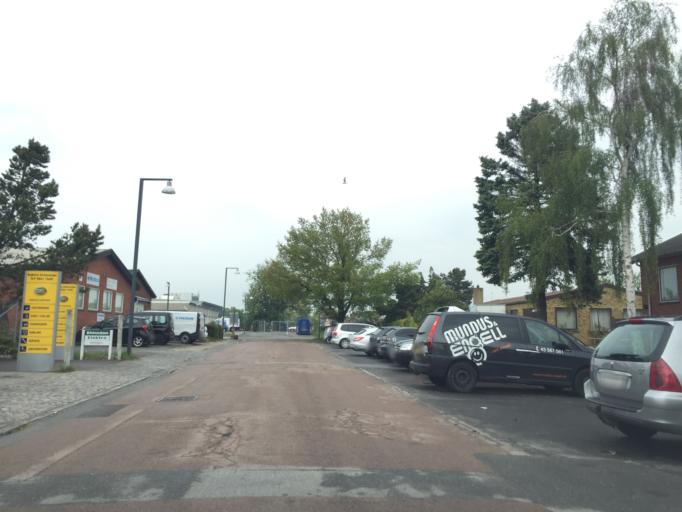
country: DK
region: Capital Region
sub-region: Rodovre Kommune
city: Rodovre
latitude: 55.6722
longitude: 12.4427
